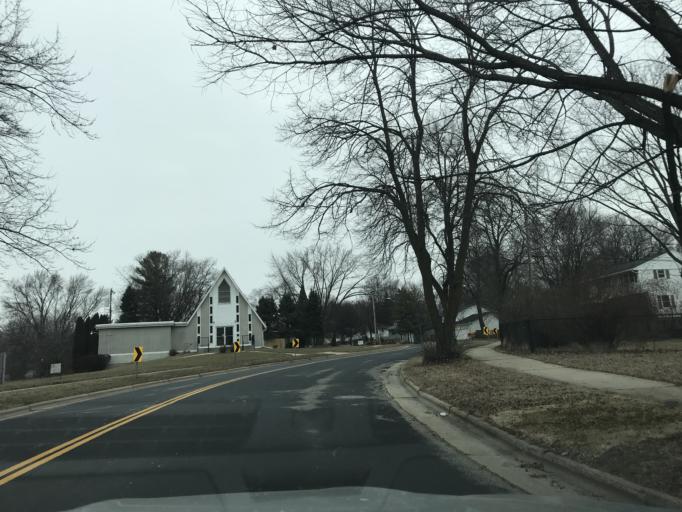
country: US
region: Wisconsin
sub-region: Dane County
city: Monona
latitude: 43.0887
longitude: -89.3027
